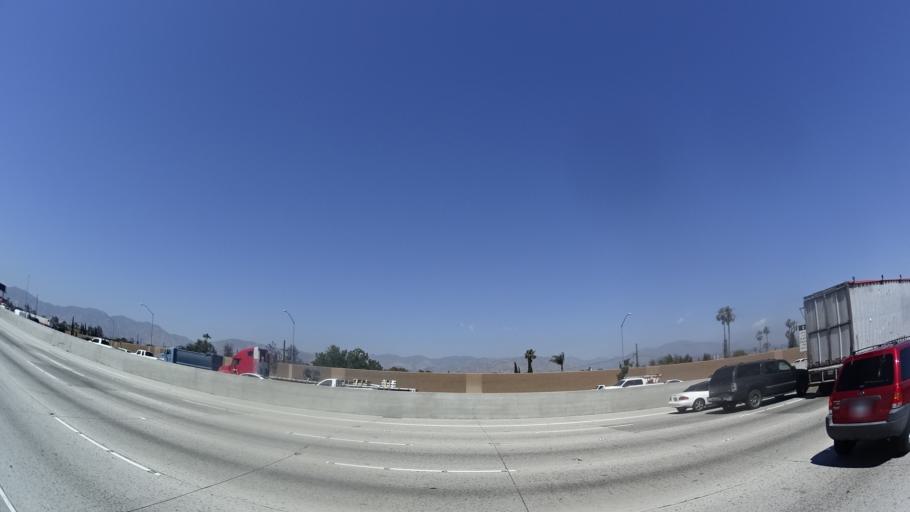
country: US
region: California
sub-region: Los Angeles County
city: San Fernando
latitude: 34.2428
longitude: -118.4208
